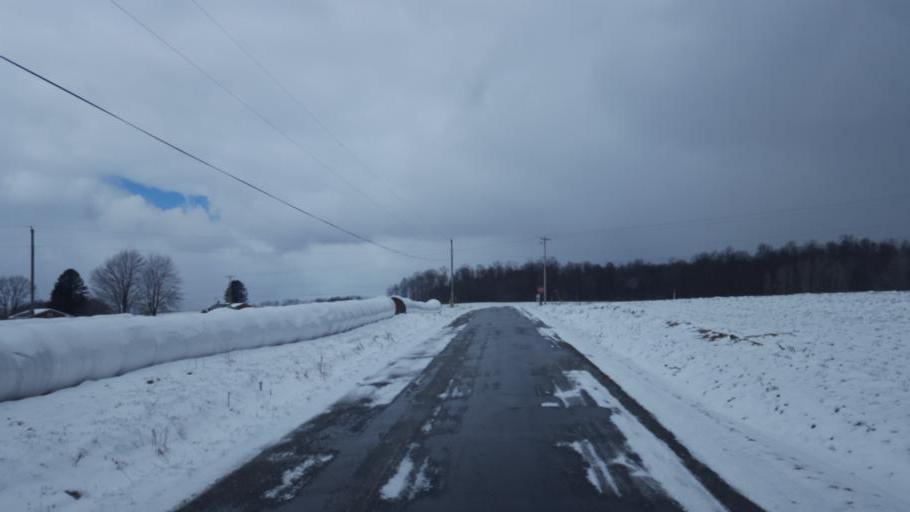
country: US
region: Pennsylvania
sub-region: Mercer County
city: Stoneboro
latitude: 41.4102
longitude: -80.1004
